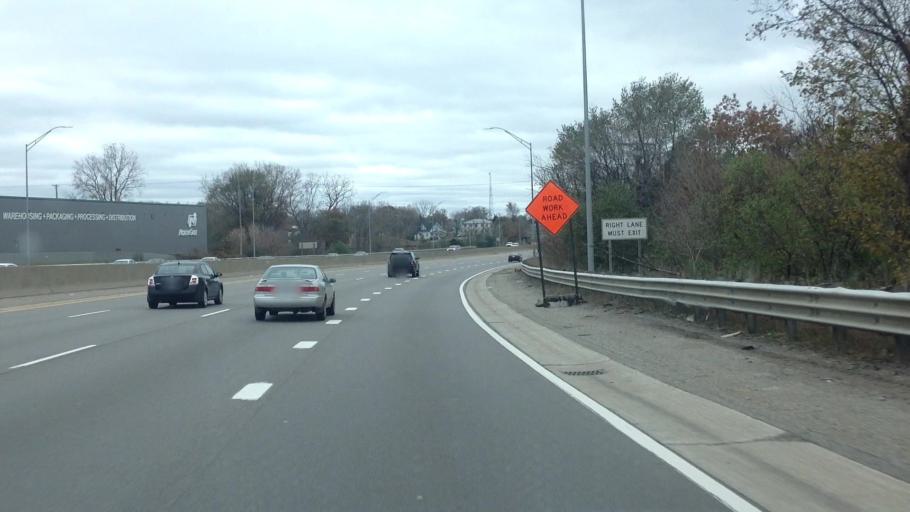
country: US
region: Michigan
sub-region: Genesee County
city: Flint
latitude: 43.0110
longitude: -83.6662
